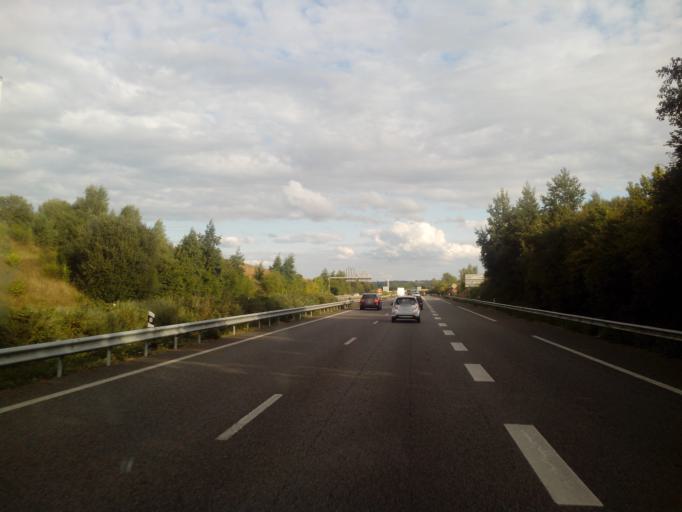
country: FR
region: Brittany
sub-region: Departement d'Ille-et-Vilaine
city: Fouillard
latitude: 48.1464
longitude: -1.5920
